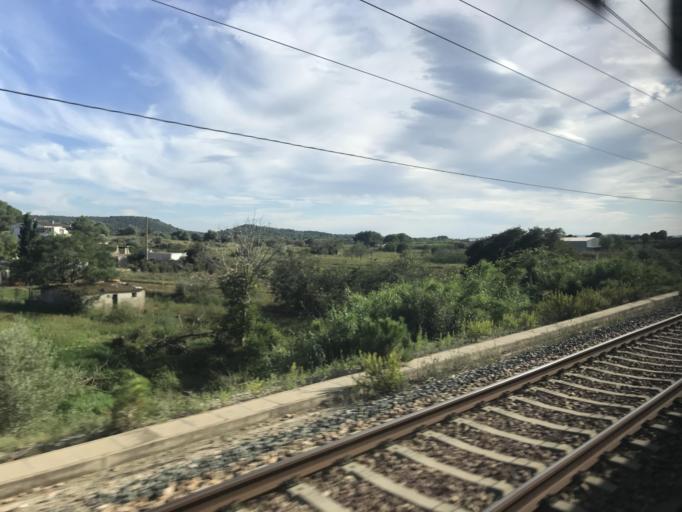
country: ES
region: Catalonia
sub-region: Provincia de Tarragona
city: Ulldecona
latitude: 40.5877
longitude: 0.4406
